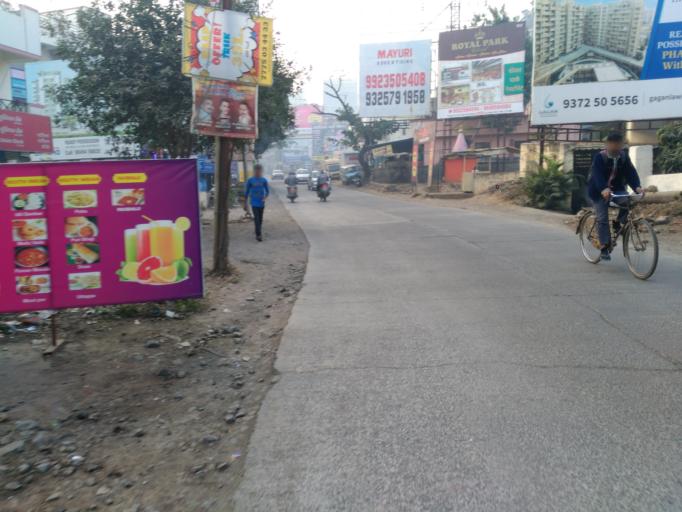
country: IN
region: Maharashtra
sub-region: Pune Division
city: Pune
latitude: 18.4579
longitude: 73.9124
